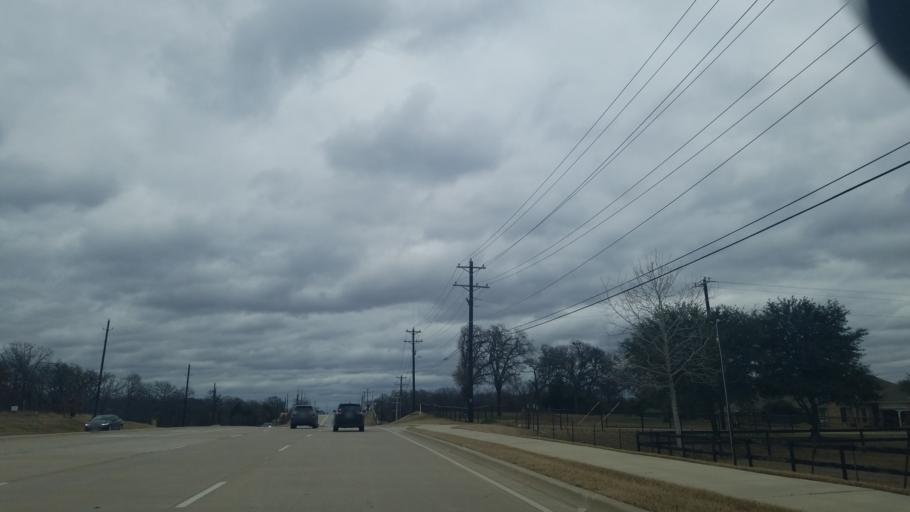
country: US
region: Texas
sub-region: Denton County
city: Bartonville
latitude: 33.0433
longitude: -97.1609
